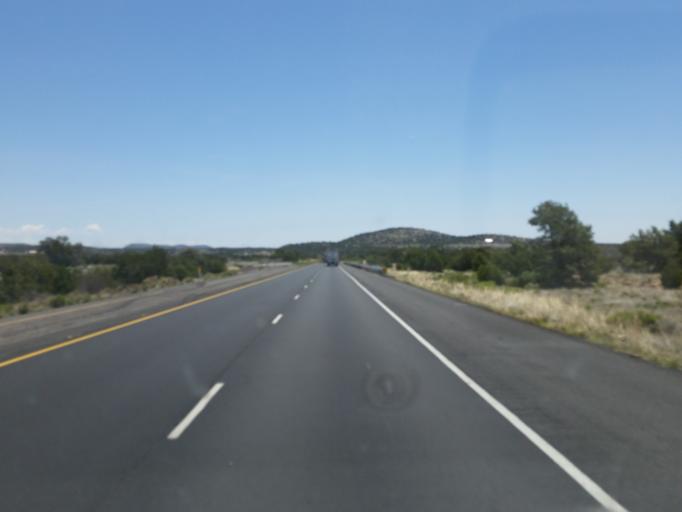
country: US
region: Arizona
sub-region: Coconino County
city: Flagstaff
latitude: 35.2014
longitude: -111.4378
